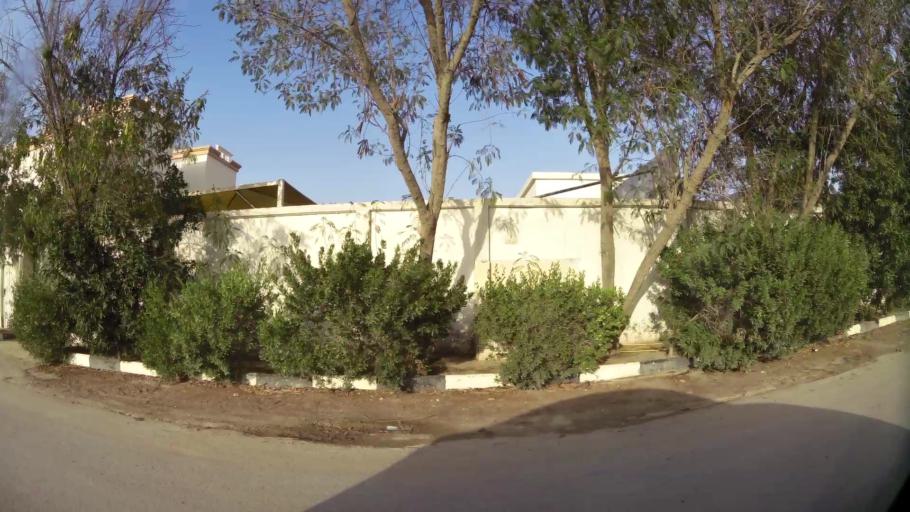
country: QA
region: Baladiyat ar Rayyan
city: Ar Rayyan
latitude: 25.3259
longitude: 51.4519
